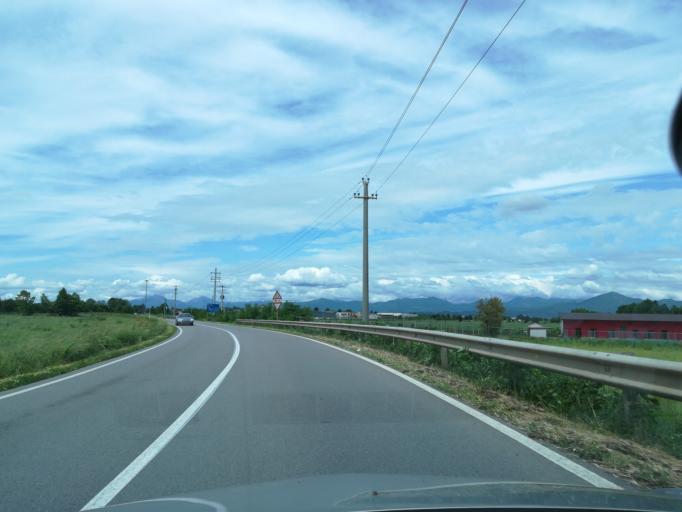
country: IT
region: Lombardy
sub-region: Provincia di Bergamo
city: Mornico al Serio
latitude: 45.5817
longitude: 9.8184
